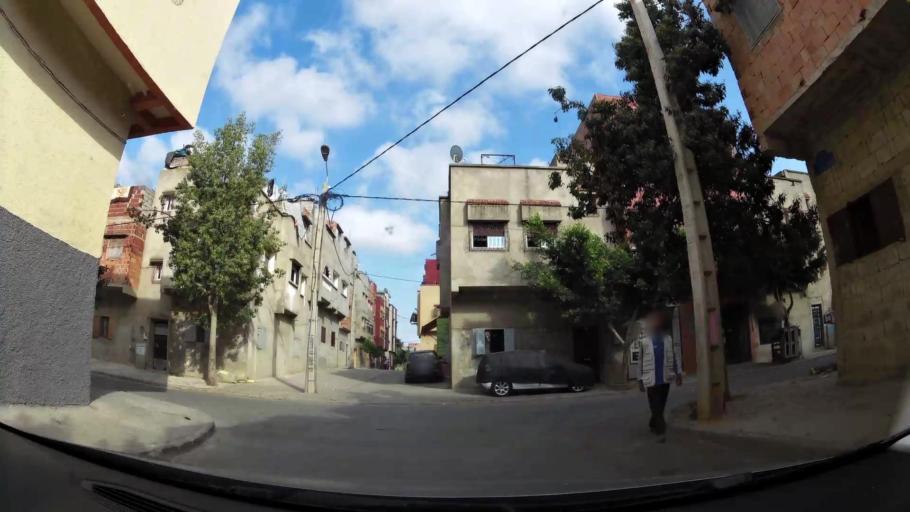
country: MA
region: Rabat-Sale-Zemmour-Zaer
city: Sale
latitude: 34.0575
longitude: -6.7749
